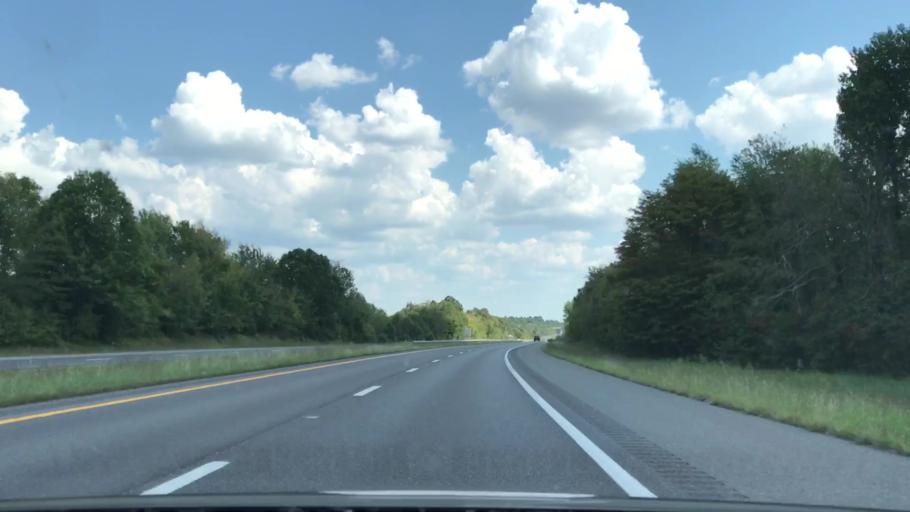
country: US
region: Kentucky
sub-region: Lyon County
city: Eddyville
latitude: 37.1098
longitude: -88.0216
